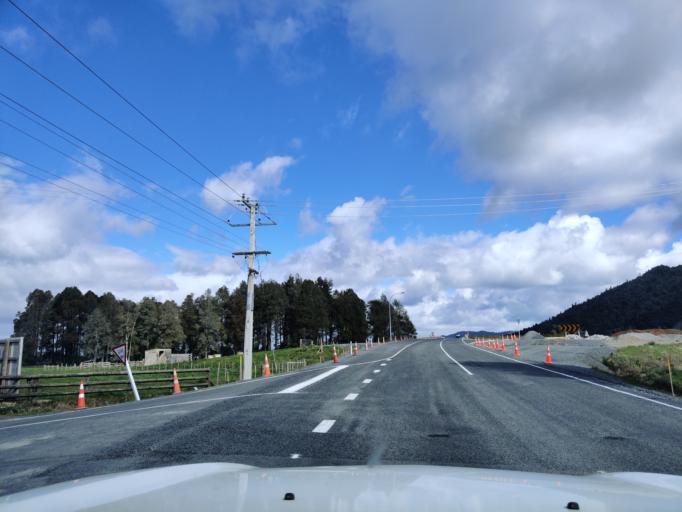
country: NZ
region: Waikato
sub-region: Waikato District
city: Ngaruawahia
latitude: -37.5945
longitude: 175.2073
